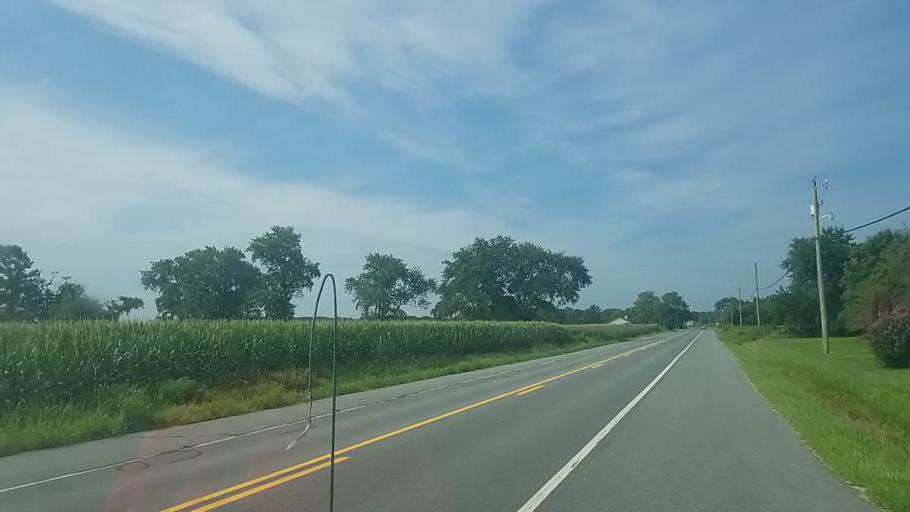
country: US
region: Delaware
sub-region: Sussex County
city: Selbyville
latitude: 38.5359
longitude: -75.1869
